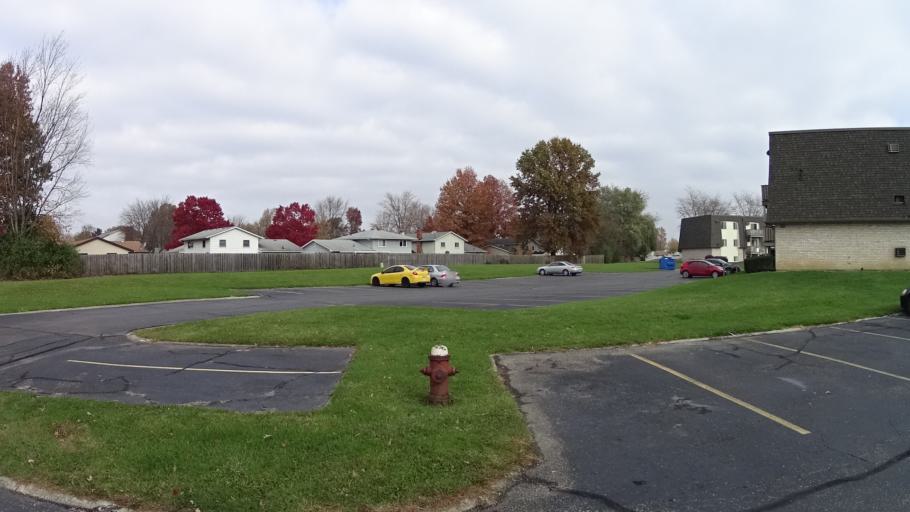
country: US
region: Ohio
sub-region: Lorain County
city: Elyria
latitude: 41.3531
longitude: -82.0809
